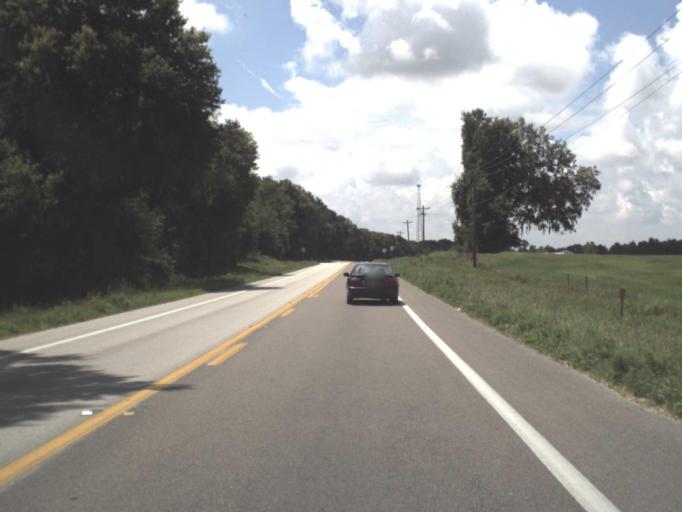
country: US
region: Florida
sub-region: Gilchrist County
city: Trenton
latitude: 29.7467
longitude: -82.8593
